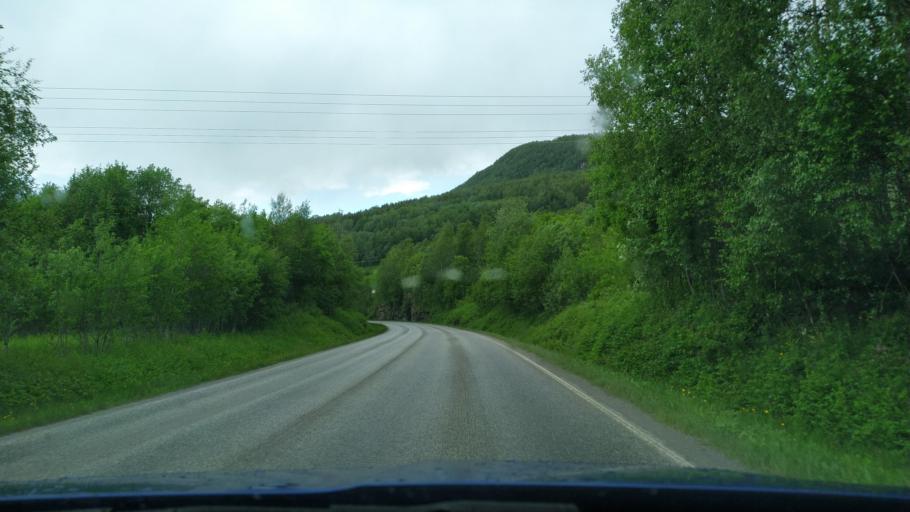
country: NO
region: Troms
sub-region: Sorreisa
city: Sorreisa
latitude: 69.1567
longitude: 18.1609
